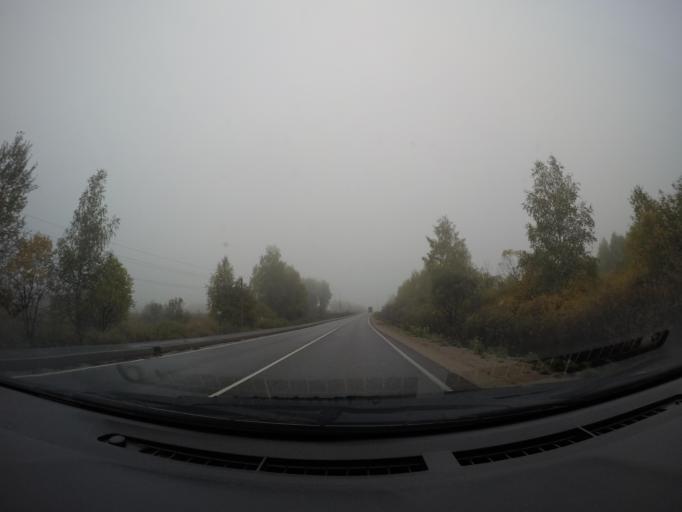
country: RU
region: Moskovskaya
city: Rumyantsevo
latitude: 55.8441
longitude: 36.4847
